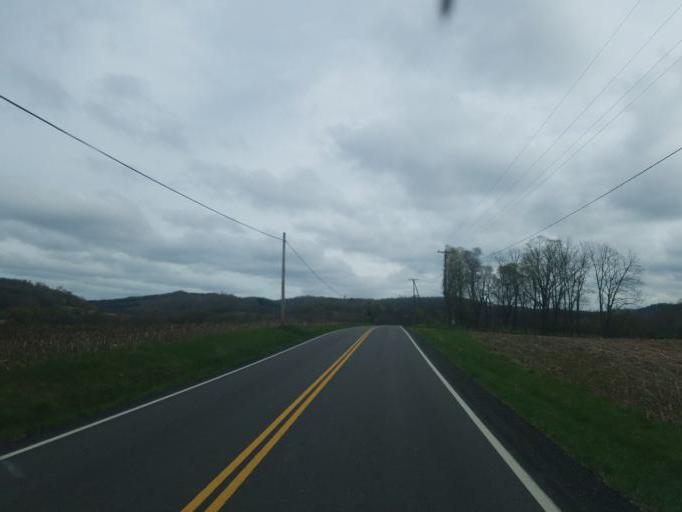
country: US
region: Ohio
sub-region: Knox County
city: Danville
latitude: 40.5053
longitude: -82.2185
